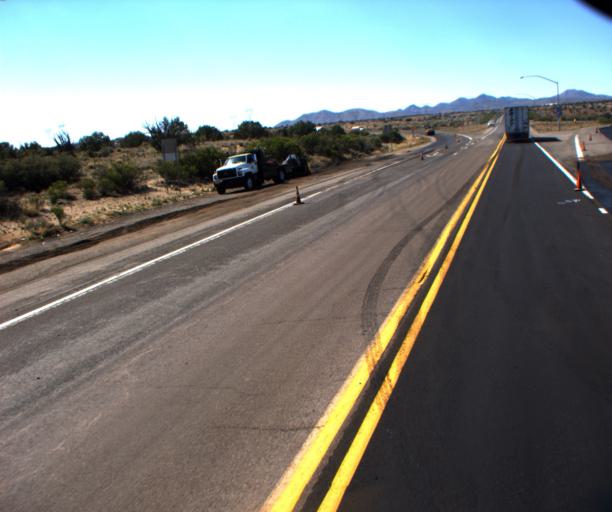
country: US
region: Arizona
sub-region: Mohave County
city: New Kingman-Butler
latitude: 35.1560
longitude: -113.6943
